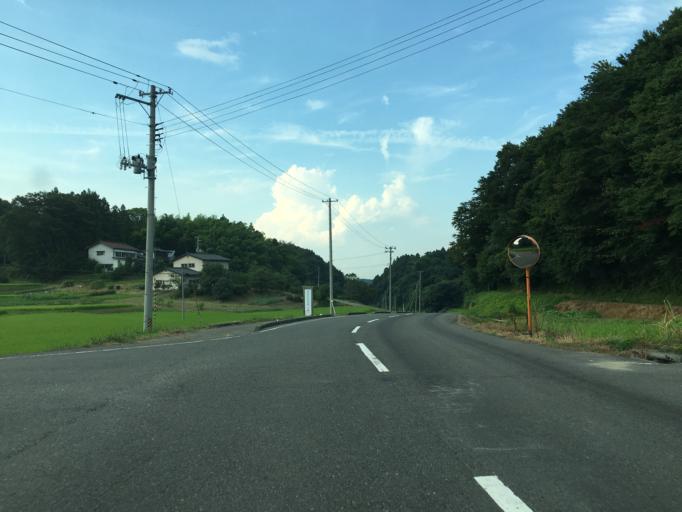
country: JP
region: Fukushima
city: Motomiya
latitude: 37.5354
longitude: 140.4413
